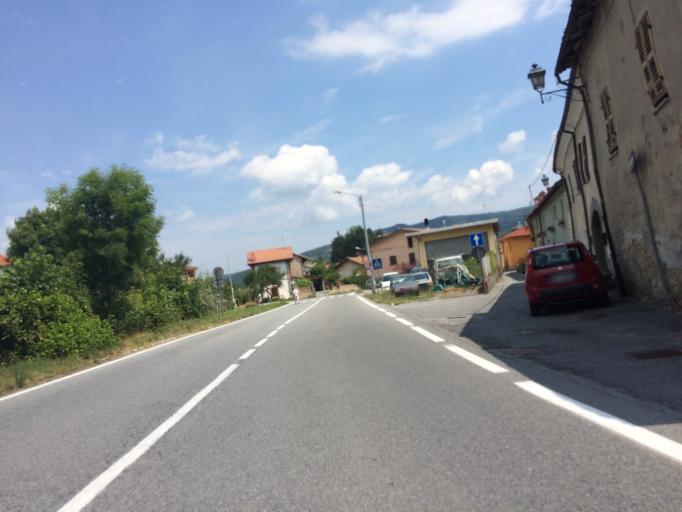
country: IT
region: Piedmont
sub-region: Provincia di Cuneo
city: Bagnasco
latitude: 44.2978
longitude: 8.0427
